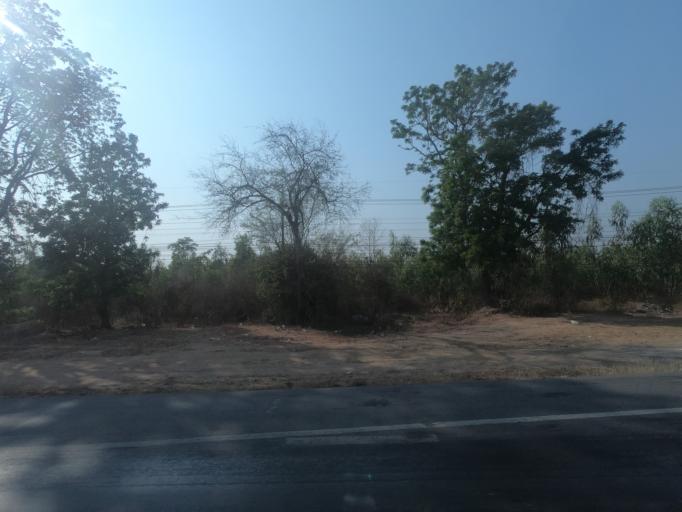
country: TH
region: Khon Kaen
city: Ban Haet
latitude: 16.2332
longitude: 102.7674
